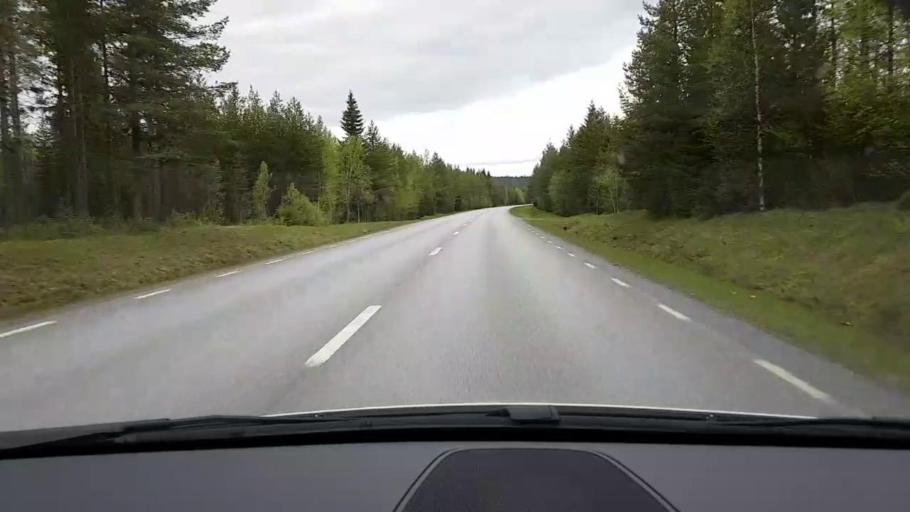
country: SE
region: Jaemtland
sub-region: Krokoms Kommun
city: Valla
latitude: 63.2852
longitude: 13.9295
